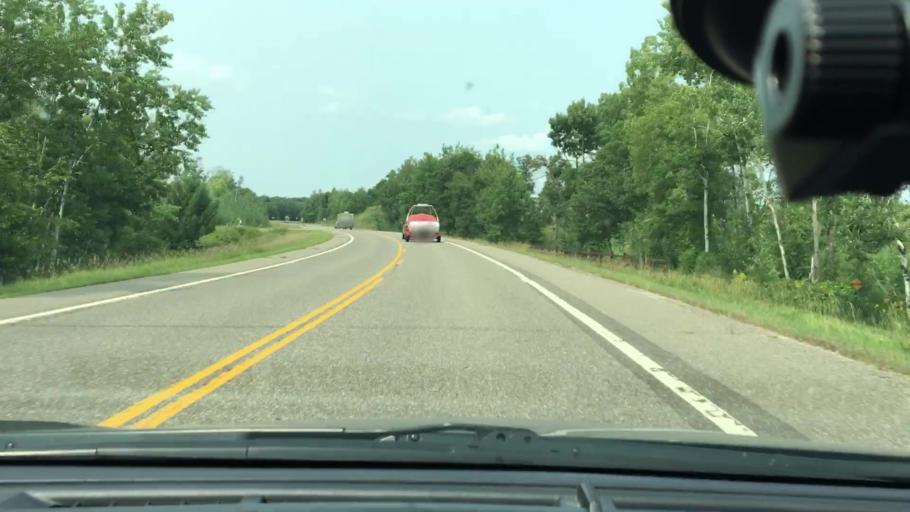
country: US
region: Minnesota
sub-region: Cass County
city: East Gull Lake
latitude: 46.4022
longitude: -94.3510
